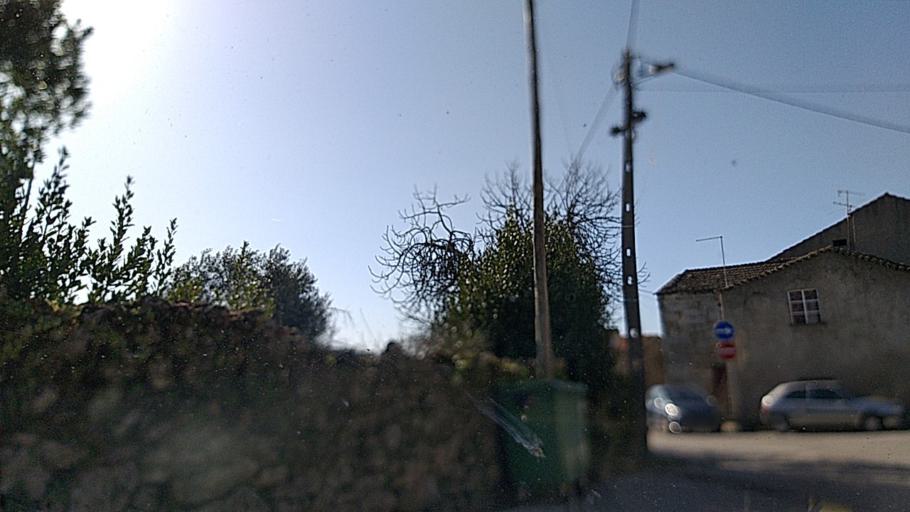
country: PT
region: Guarda
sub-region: Celorico da Beira
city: Celorico da Beira
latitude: 40.6752
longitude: -7.3971
